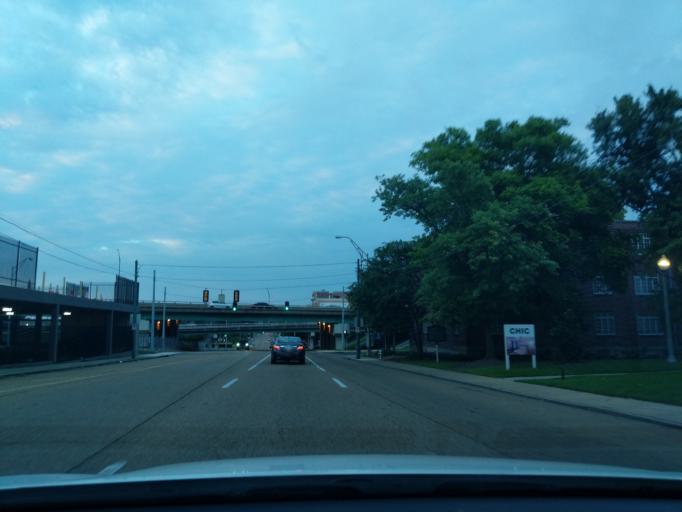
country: US
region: Tennessee
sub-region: Shelby County
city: Memphis
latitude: 35.1518
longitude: -90.0474
